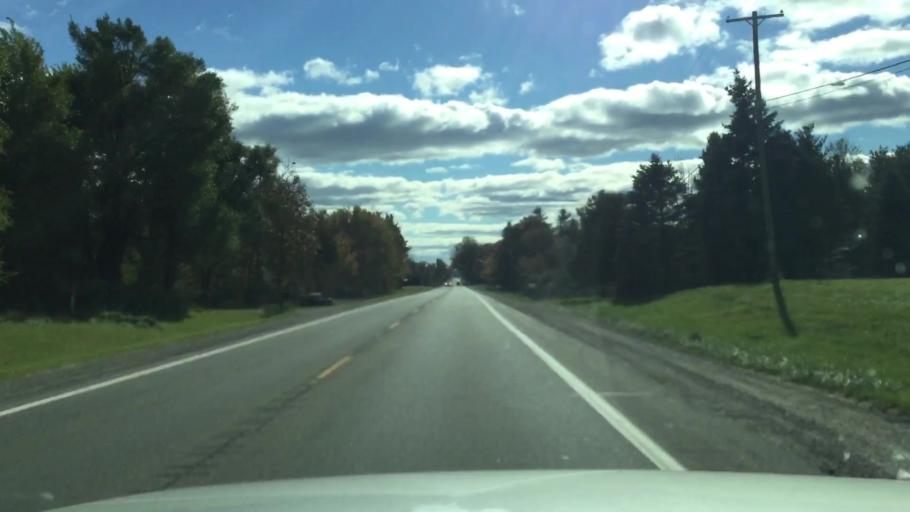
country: US
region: Michigan
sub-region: Lapeer County
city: Lapeer
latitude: 43.1143
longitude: -83.3092
